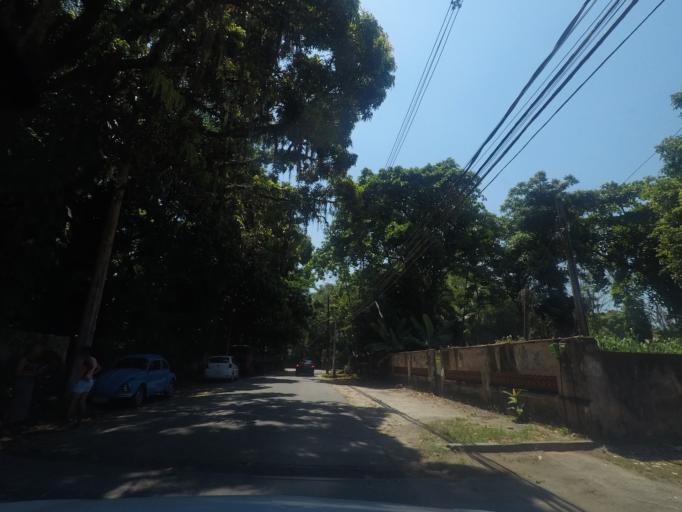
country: BR
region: Rio de Janeiro
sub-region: Nilopolis
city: Nilopolis
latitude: -22.9802
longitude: -43.4600
